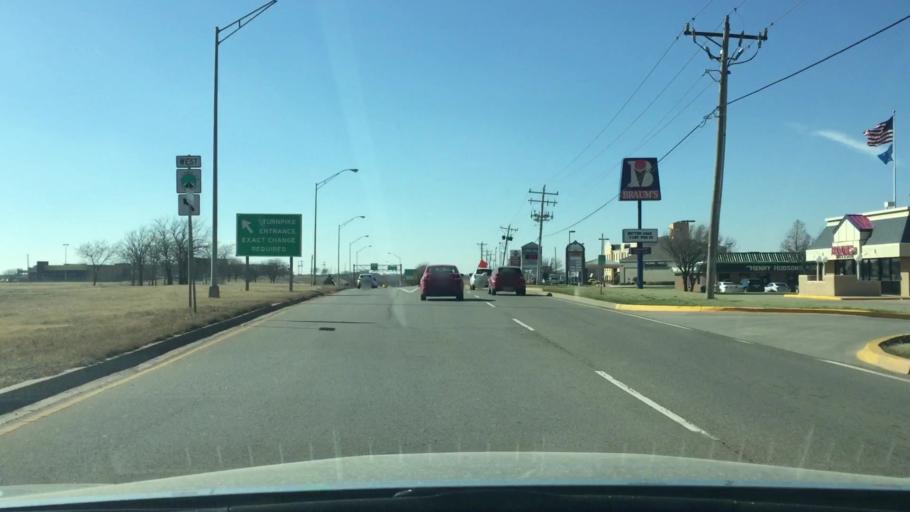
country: US
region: Oklahoma
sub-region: Oklahoma County
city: The Village
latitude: 35.6091
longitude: -97.5324
